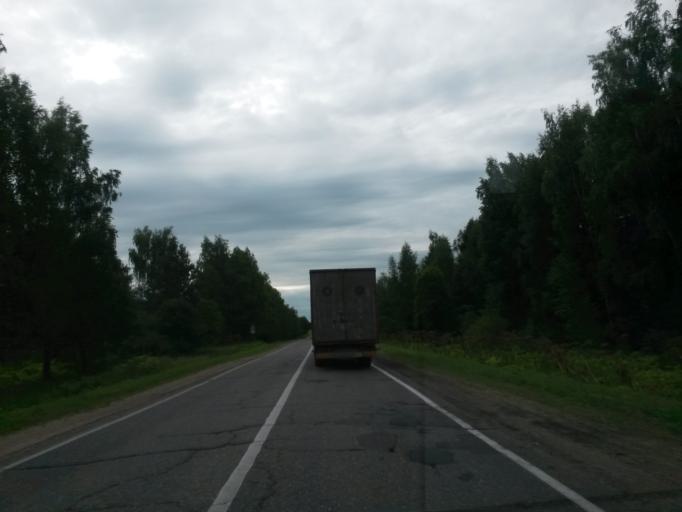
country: RU
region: Jaroslavl
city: Krasnyye Tkachi
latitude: 57.3650
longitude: 39.7411
